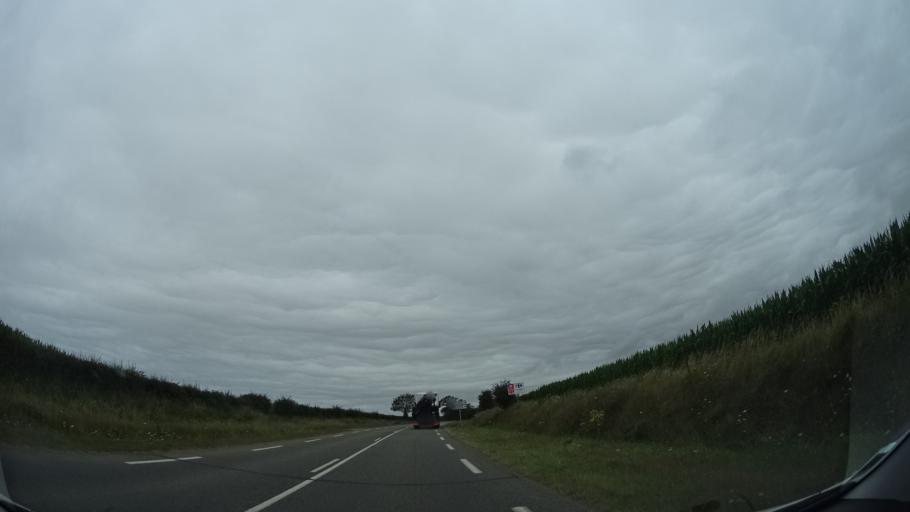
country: FR
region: Lower Normandy
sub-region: Departement de la Manche
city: Portbail
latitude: 49.3670
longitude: -1.7198
